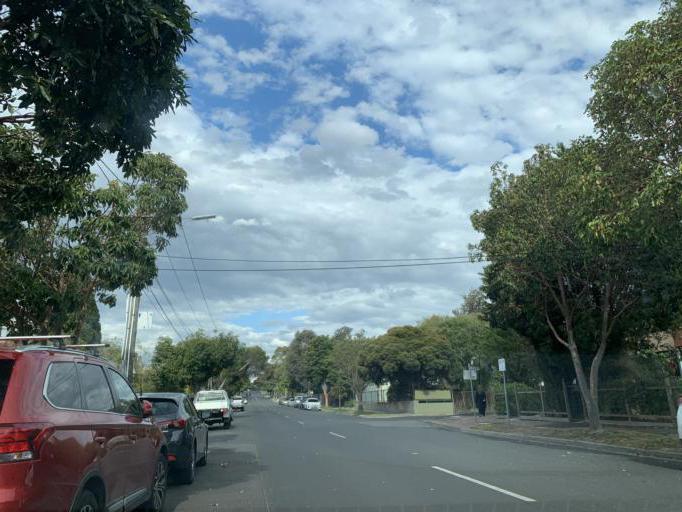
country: AU
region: Victoria
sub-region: Bayside
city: Hampton
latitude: -37.9361
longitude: 144.9997
